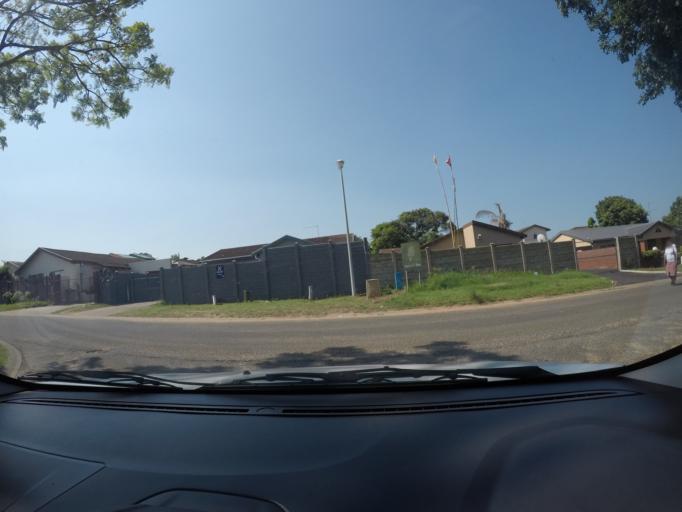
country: ZA
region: KwaZulu-Natal
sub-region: uThungulu District Municipality
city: Richards Bay
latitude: -28.7226
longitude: 32.0442
